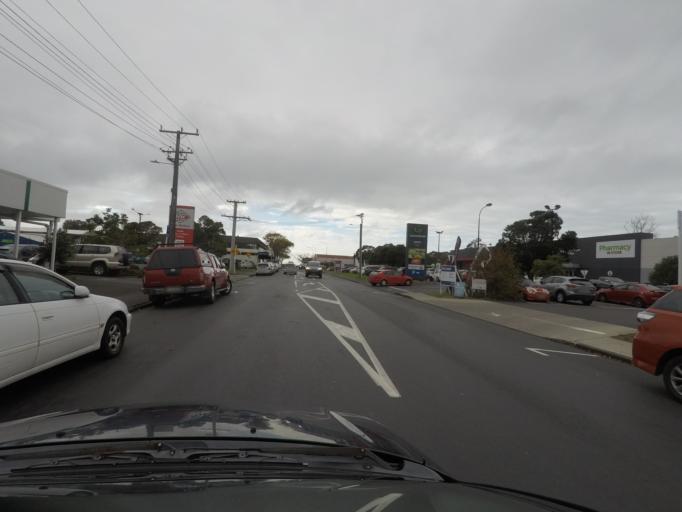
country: NZ
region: Auckland
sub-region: Auckland
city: Rothesay Bay
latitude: -36.7168
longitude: 174.7466
